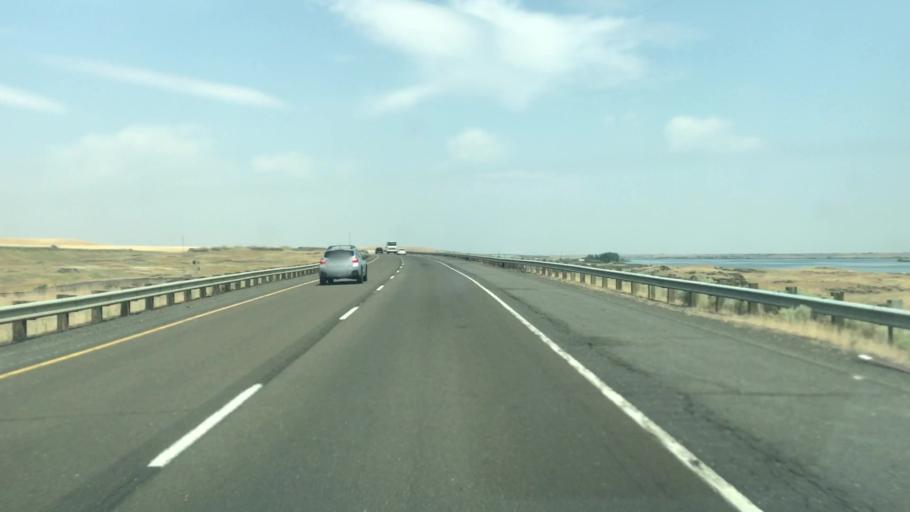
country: US
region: Washington
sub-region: Adams County
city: Ritzville
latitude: 47.2464
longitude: -118.1101
